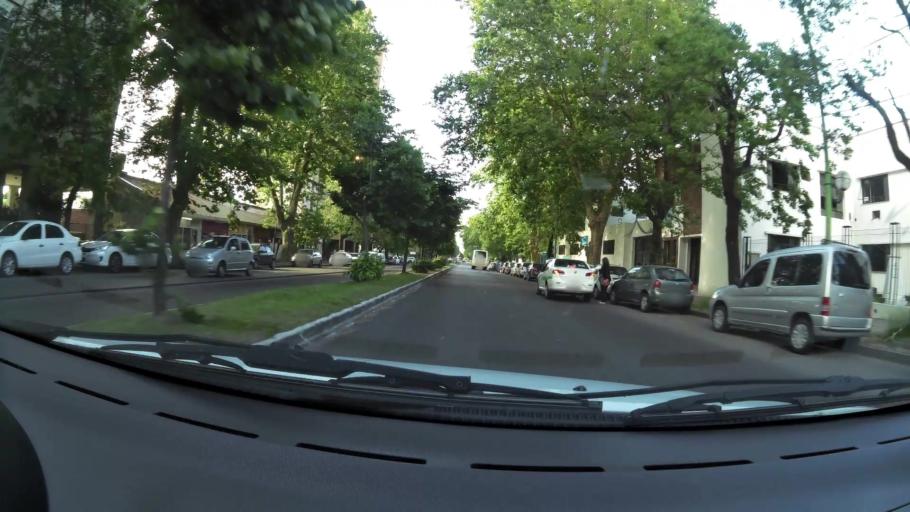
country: AR
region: Buenos Aires
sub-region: Partido de La Plata
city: La Plata
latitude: -34.9011
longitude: -57.9493
